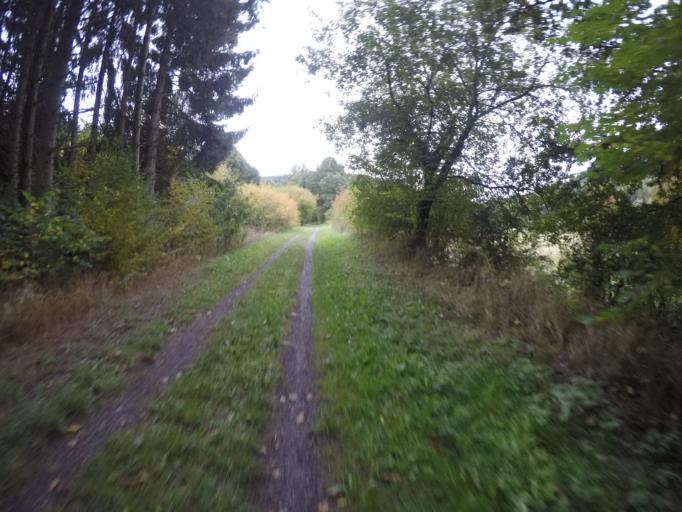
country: BE
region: Wallonia
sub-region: Province du Luxembourg
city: Fauvillers
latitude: 49.8621
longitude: 5.6942
